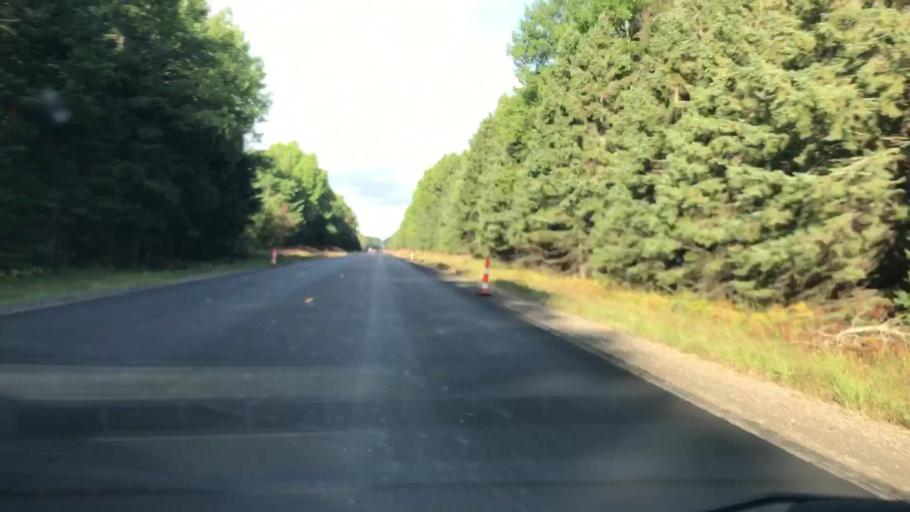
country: US
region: Michigan
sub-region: Mackinac County
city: Saint Ignace
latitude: 46.3459
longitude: -84.9366
